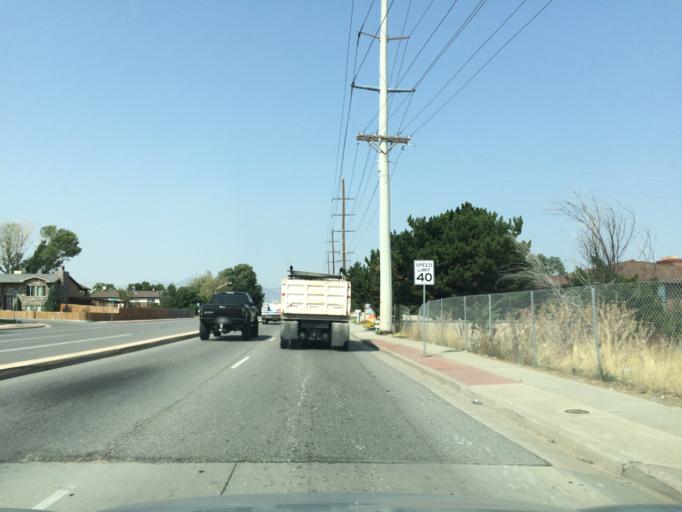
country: US
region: Utah
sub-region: Salt Lake County
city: South Jordan Heights
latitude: 40.5879
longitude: -111.9781
